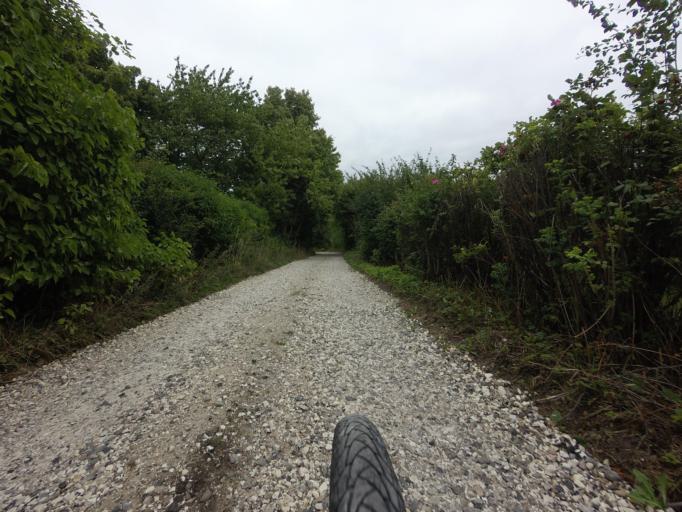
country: DK
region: Zealand
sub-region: Stevns Kommune
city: Store Heddinge
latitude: 55.3399
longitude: 12.4439
